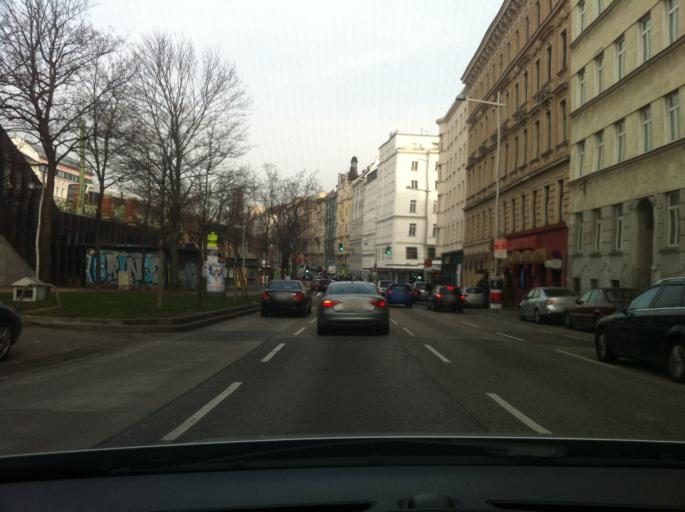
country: AT
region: Vienna
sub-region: Wien Stadt
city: Vienna
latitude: 48.2077
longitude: 16.3384
